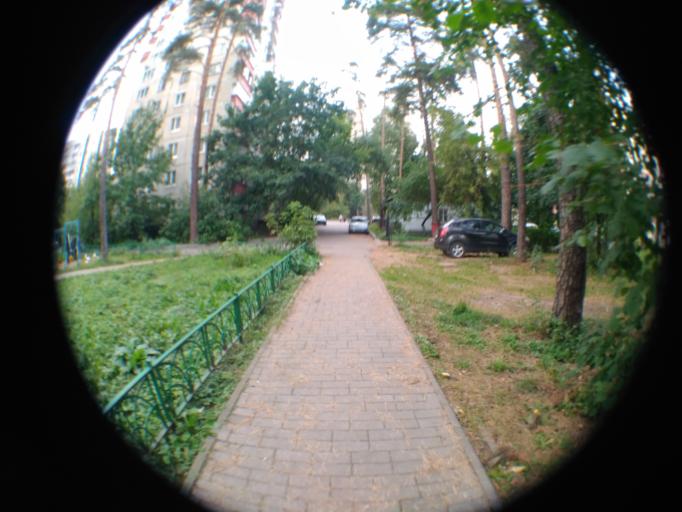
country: RU
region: Moskovskaya
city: Zhukovskiy
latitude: 55.5820
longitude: 38.1437
